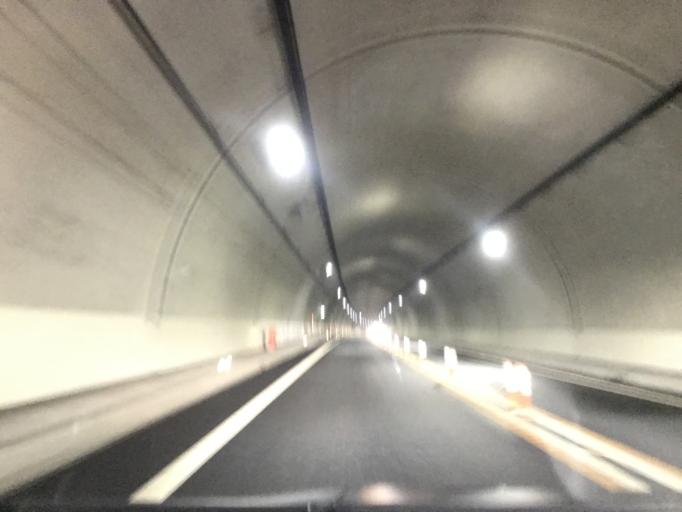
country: JP
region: Fukuoka
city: Kanda
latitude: 33.7893
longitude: 130.9705
